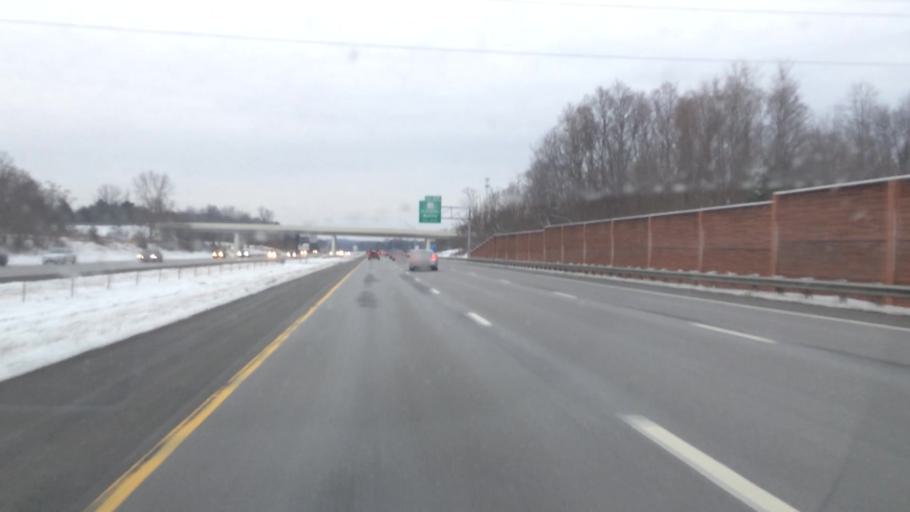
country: US
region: Ohio
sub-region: Medina County
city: Brunswick
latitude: 41.2174
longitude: -81.7937
